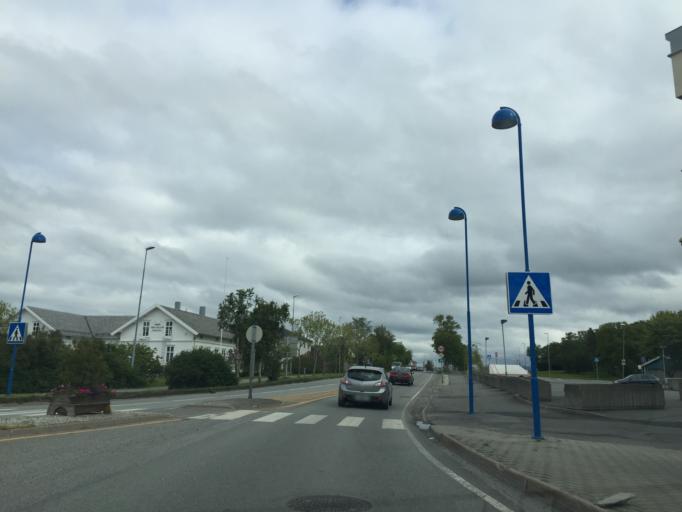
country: NO
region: Nordland
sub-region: Bodo
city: Bodo
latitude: 67.2858
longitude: 14.4015
